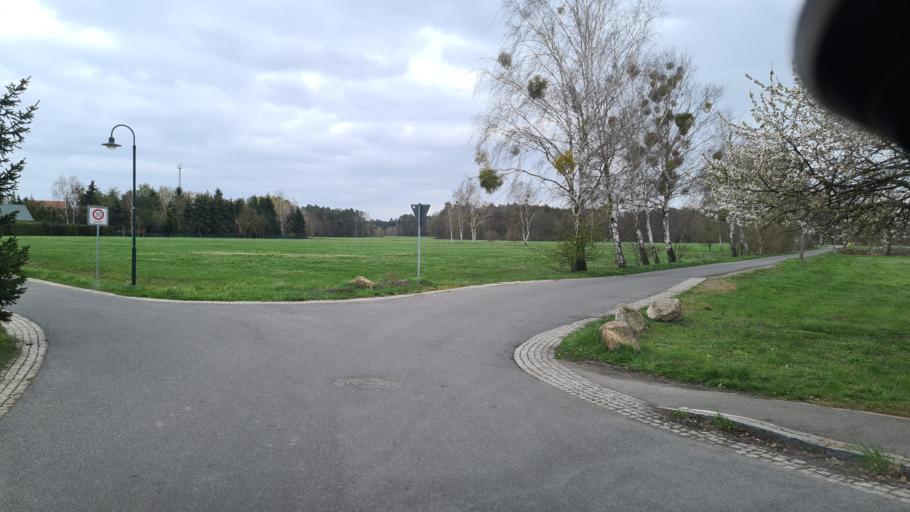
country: DE
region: Brandenburg
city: Hohenbocka
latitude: 51.4620
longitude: 14.0652
